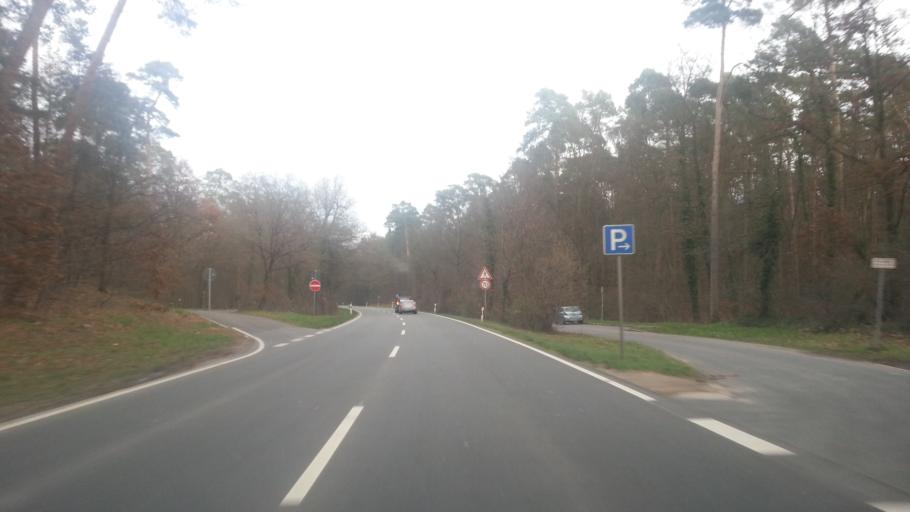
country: DE
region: Baden-Wuerttemberg
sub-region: Karlsruhe Region
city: Sandhausen
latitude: 49.3266
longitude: 8.6543
